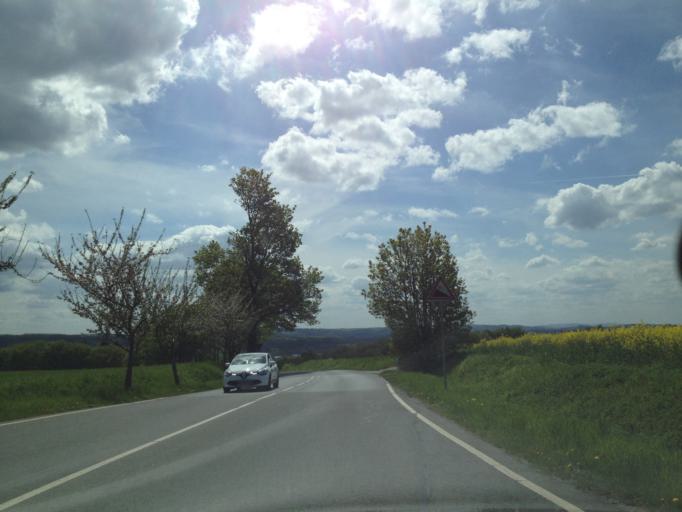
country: DE
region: North Rhine-Westphalia
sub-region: Regierungsbezirk Arnsberg
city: Mohnesee
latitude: 51.5041
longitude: 8.1350
